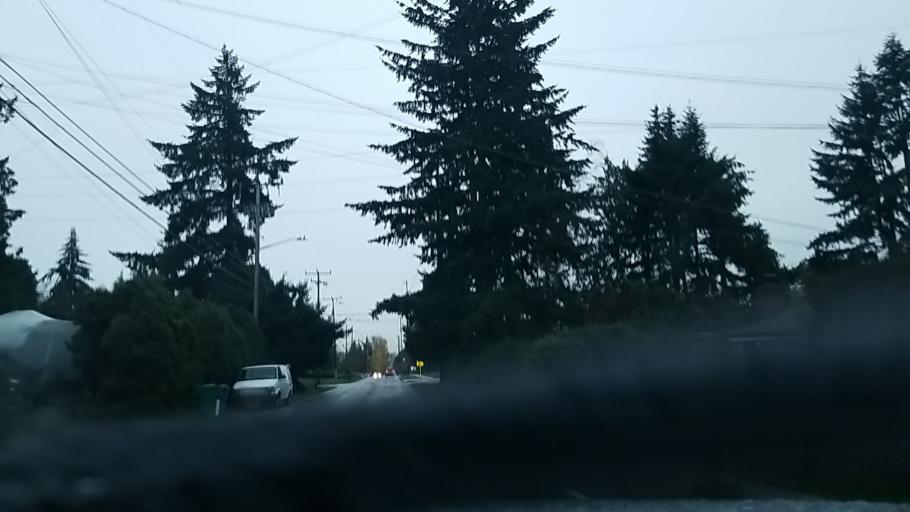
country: US
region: Washington
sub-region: King County
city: Shoreline
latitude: 47.7166
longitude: -122.3289
